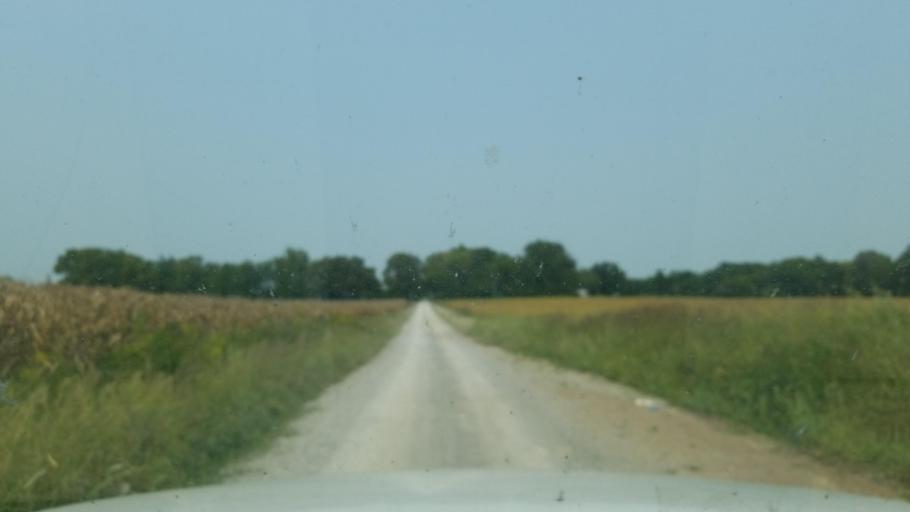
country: US
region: Illinois
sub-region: Saline County
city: Eldorado
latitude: 37.8210
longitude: -88.5167
